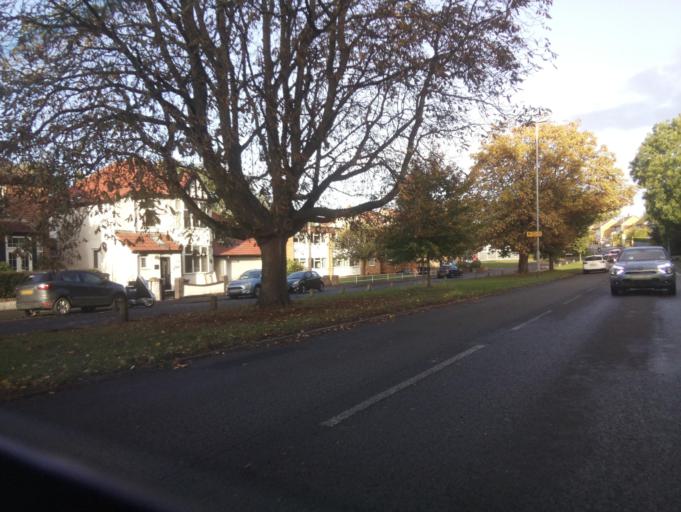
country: GB
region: England
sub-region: Bristol
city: Bristol
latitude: 51.4943
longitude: -2.6253
